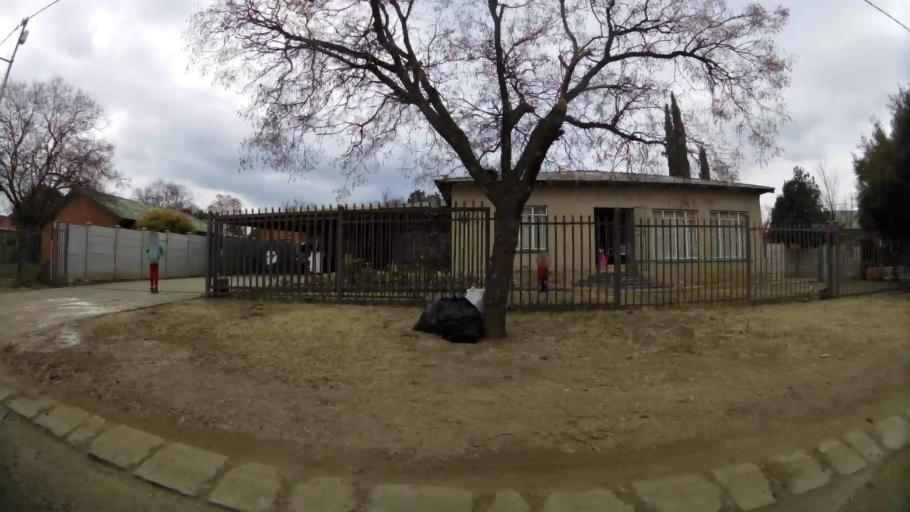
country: ZA
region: Orange Free State
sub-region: Fezile Dabi District Municipality
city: Kroonstad
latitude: -27.6840
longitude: 27.2285
